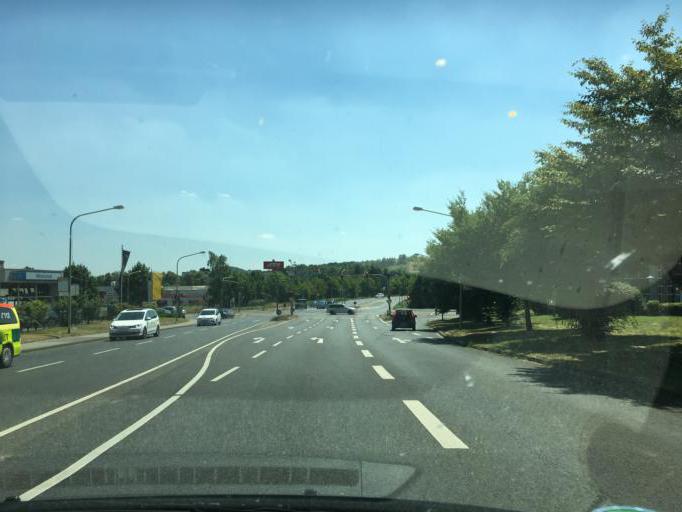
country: DE
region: North Rhine-Westphalia
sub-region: Regierungsbezirk Koln
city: Eschweiler
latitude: 50.8237
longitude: 6.2471
